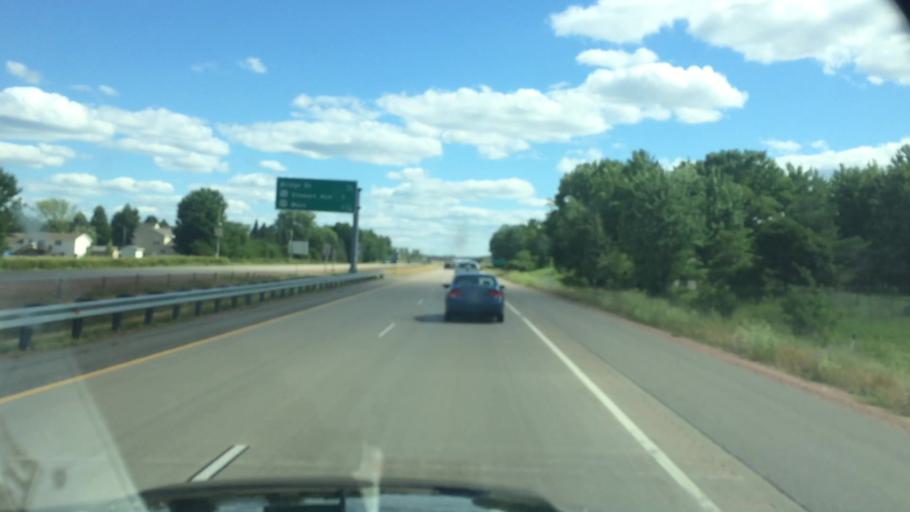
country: US
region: Wisconsin
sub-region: Marathon County
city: Wausau
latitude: 44.9787
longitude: -89.6575
